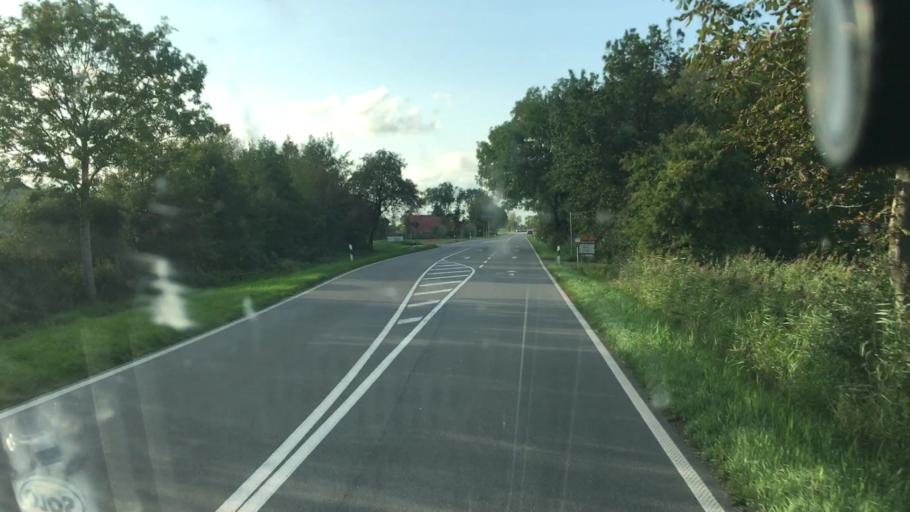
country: DE
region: Lower Saxony
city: Jever
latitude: 53.5904
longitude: 7.8735
